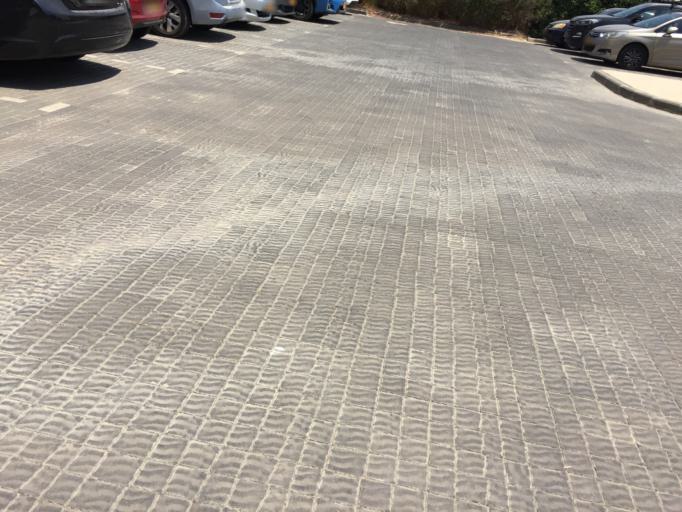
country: IL
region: Central District
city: Lod
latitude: 31.9886
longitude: 34.9089
